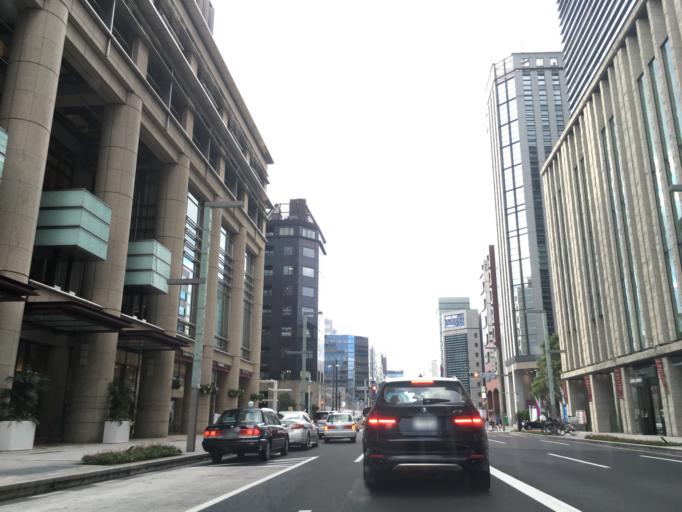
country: JP
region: Tokyo
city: Tokyo
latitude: 35.6869
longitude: 139.7738
